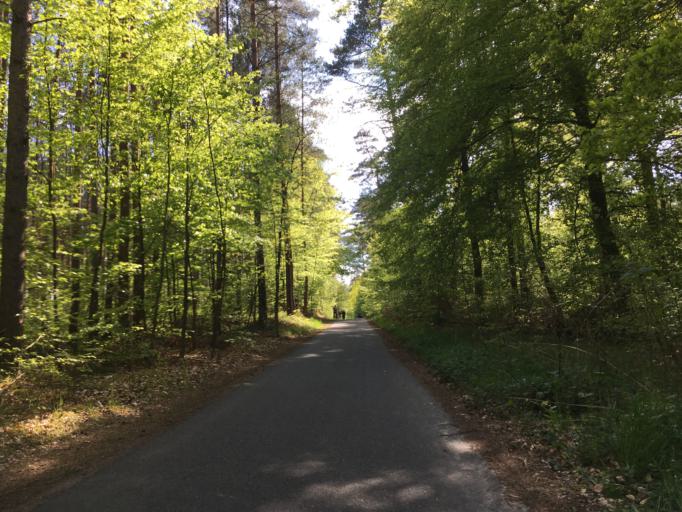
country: DE
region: Brandenburg
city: Rudnitz
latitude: 52.7382
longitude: 13.6125
